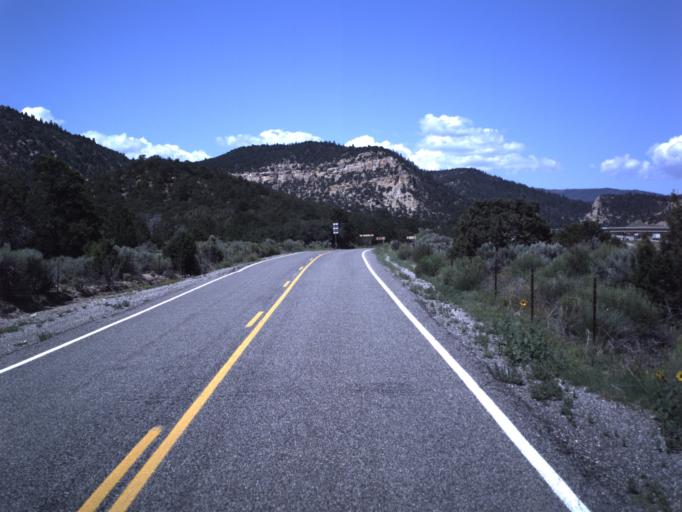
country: US
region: Utah
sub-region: Wayne County
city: Loa
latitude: 38.7567
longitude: -111.4179
